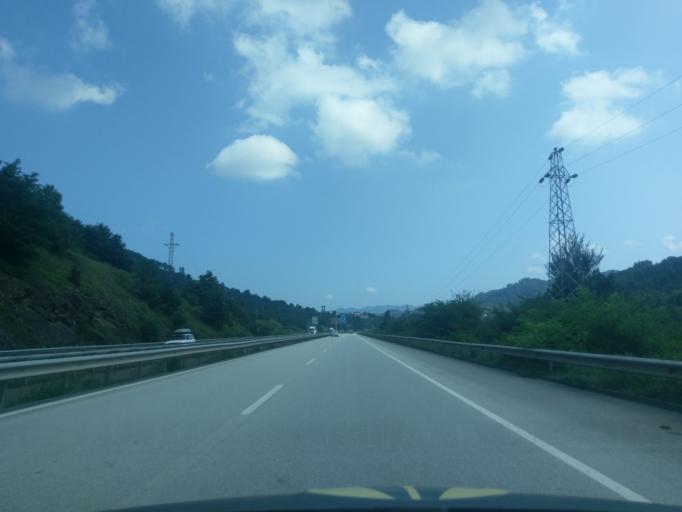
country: TR
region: Ordu
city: Persembe
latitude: 40.9777
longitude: 37.7385
